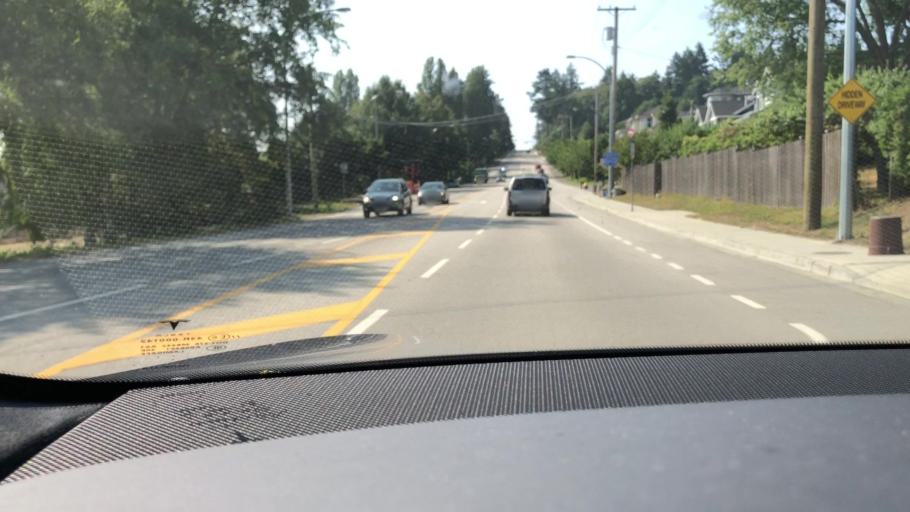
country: US
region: Washington
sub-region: Whatcom County
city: Point Roberts
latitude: 49.0097
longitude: -123.0687
